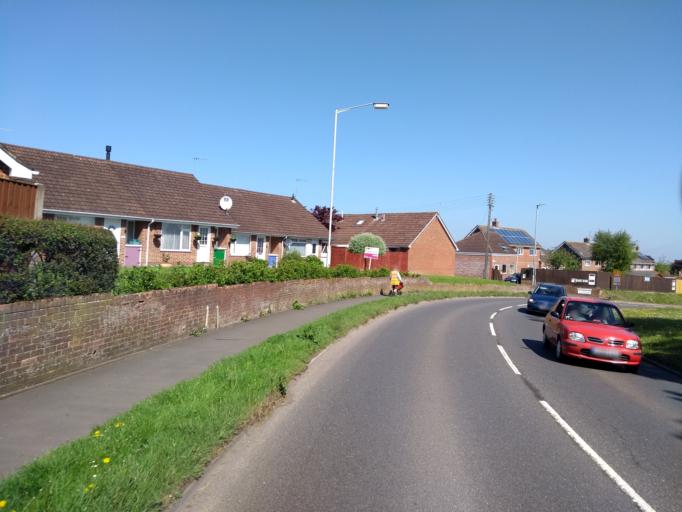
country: GB
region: England
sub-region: Somerset
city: Chard
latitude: 50.8669
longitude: -2.9642
